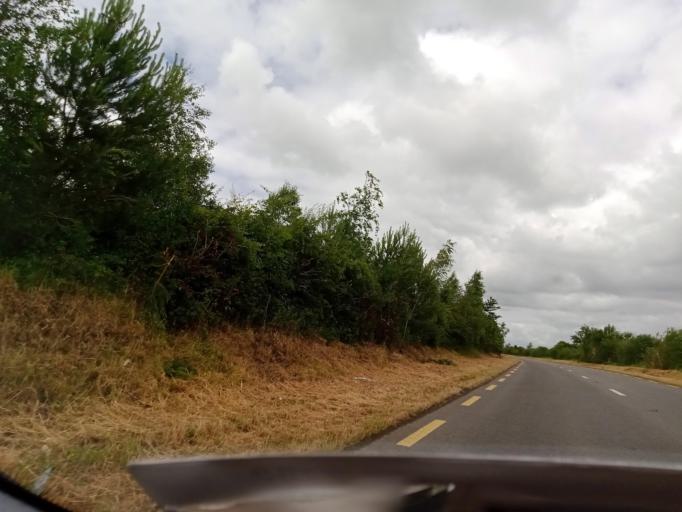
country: IE
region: Leinster
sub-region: Kilkenny
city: Thomastown
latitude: 52.4856
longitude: -7.2265
